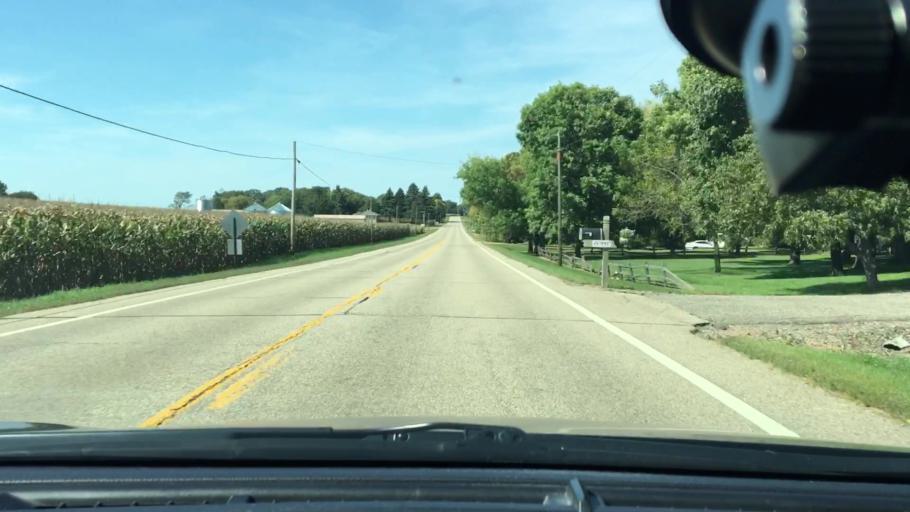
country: US
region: Minnesota
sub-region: Hennepin County
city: Corcoran
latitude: 45.1121
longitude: -93.5716
